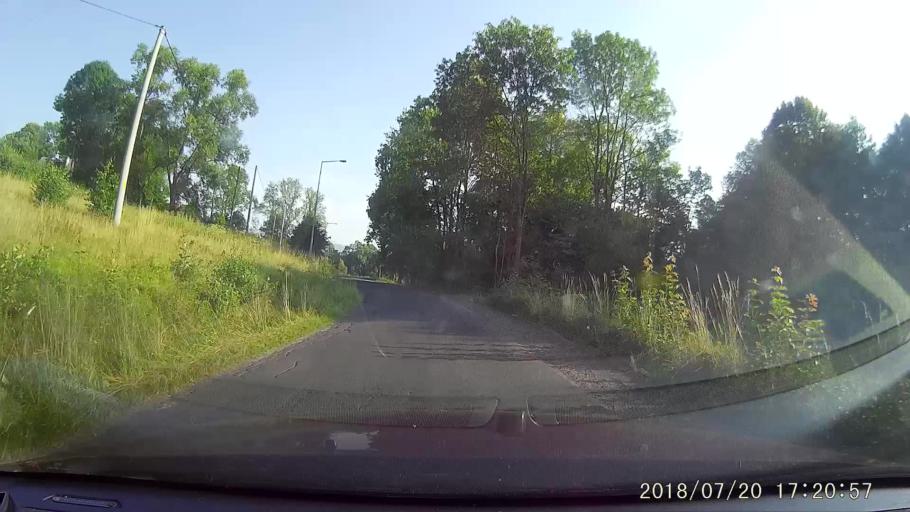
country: PL
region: Lower Silesian Voivodeship
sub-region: Powiat lubanski
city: Lesna
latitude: 50.9860
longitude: 15.2866
